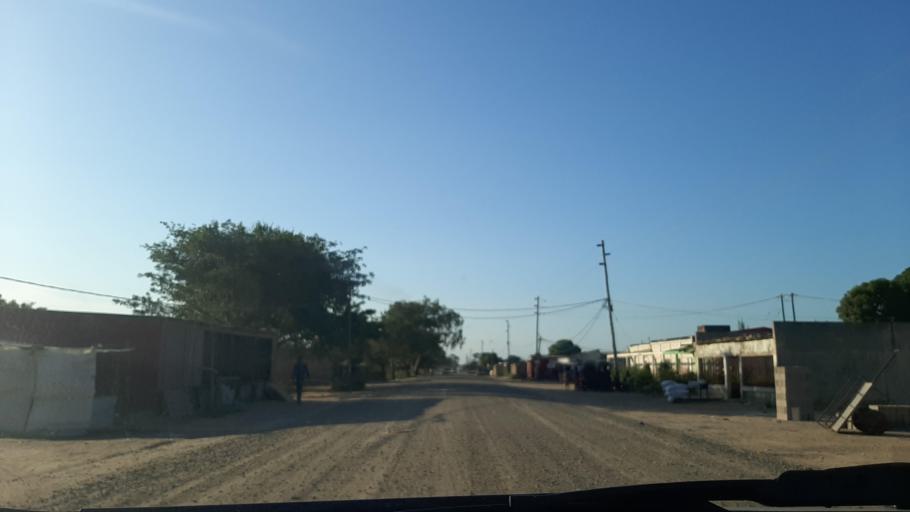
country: MZ
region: Maputo City
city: Maputo
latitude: -25.7345
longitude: 32.5372
